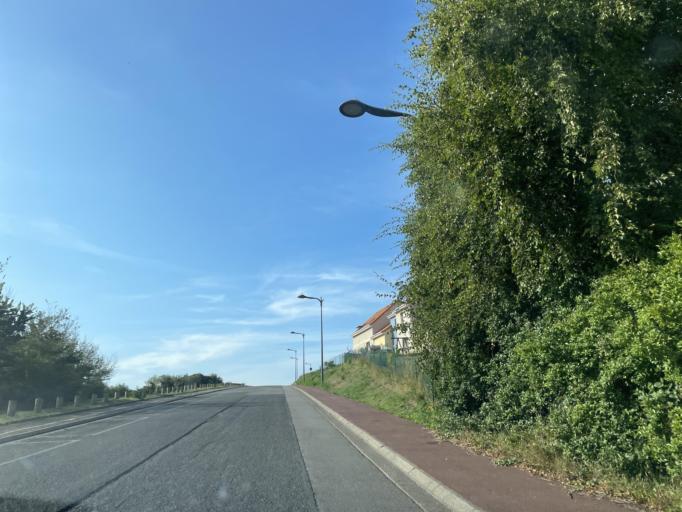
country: FR
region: Picardie
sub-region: Departement de la Somme
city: Mers-les-Bains
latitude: 50.0652
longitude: 1.3958
